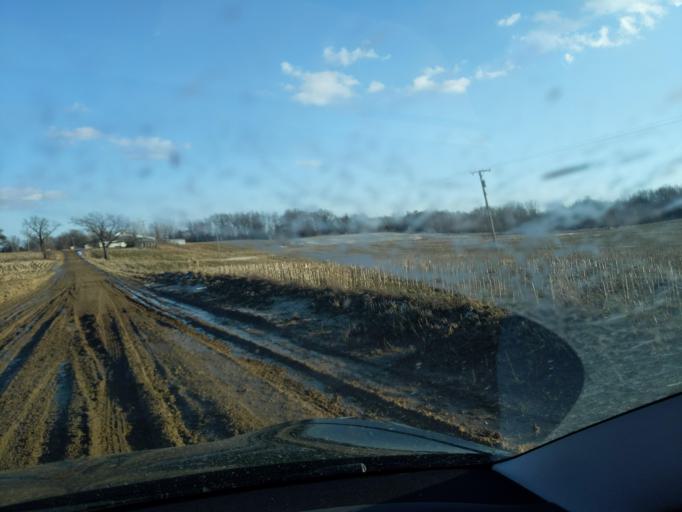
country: US
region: Michigan
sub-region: Ingham County
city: Stockbridge
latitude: 42.5222
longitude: -84.1877
